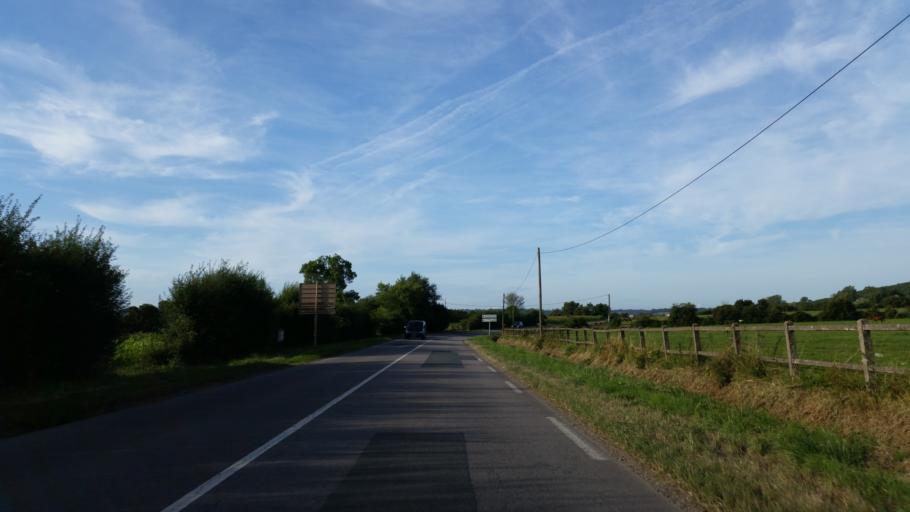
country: FR
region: Lower Normandy
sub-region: Departement du Calvados
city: Cambremer
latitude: 49.1542
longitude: -0.0072
